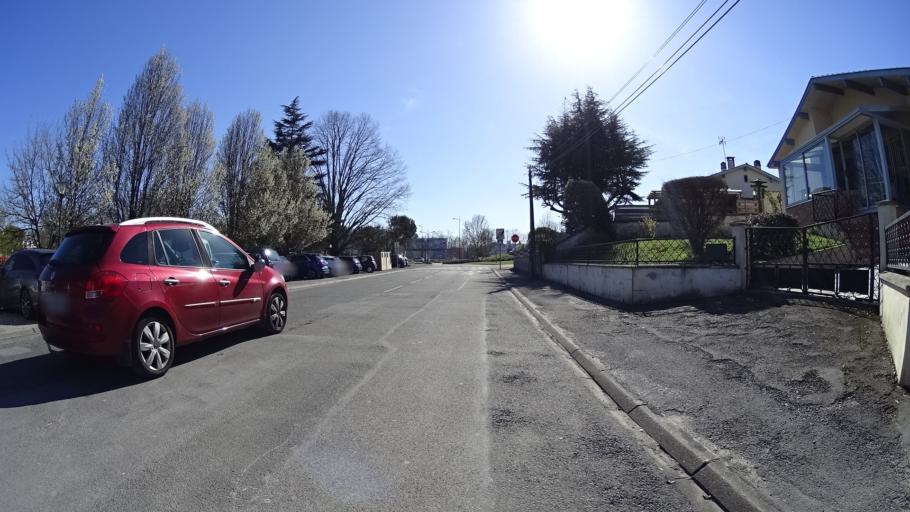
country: FR
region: Aquitaine
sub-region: Departement des Landes
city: Saint-Paul-les-Dax
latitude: 43.7267
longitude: -1.0685
